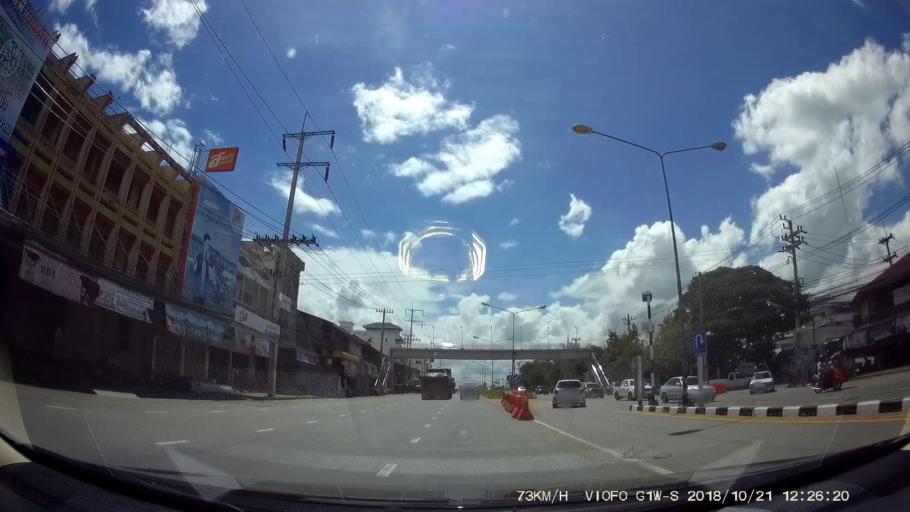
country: TH
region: Nakhon Ratchasima
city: Dan Khun Thot
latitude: 15.2109
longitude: 101.7680
